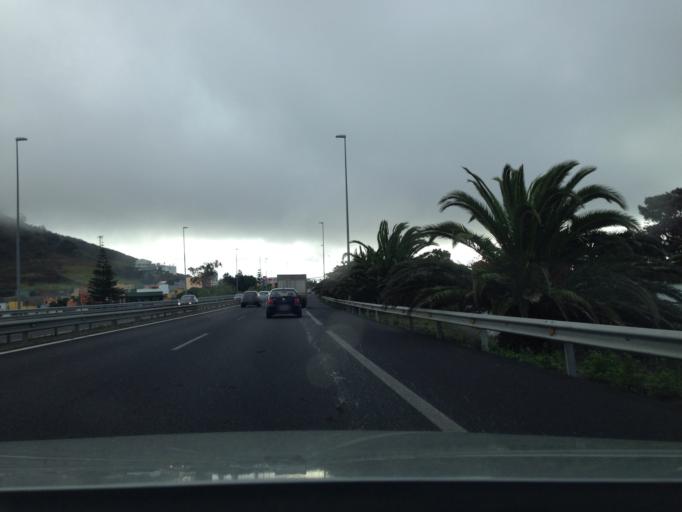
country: ES
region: Canary Islands
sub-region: Provincia de Santa Cruz de Tenerife
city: La Laguna
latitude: 28.4909
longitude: -16.3577
